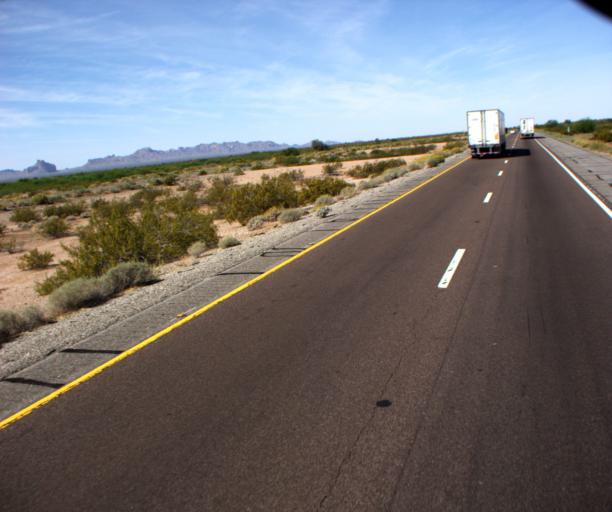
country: US
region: Arizona
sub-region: La Paz County
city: Salome
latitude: 33.5474
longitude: -113.2088
